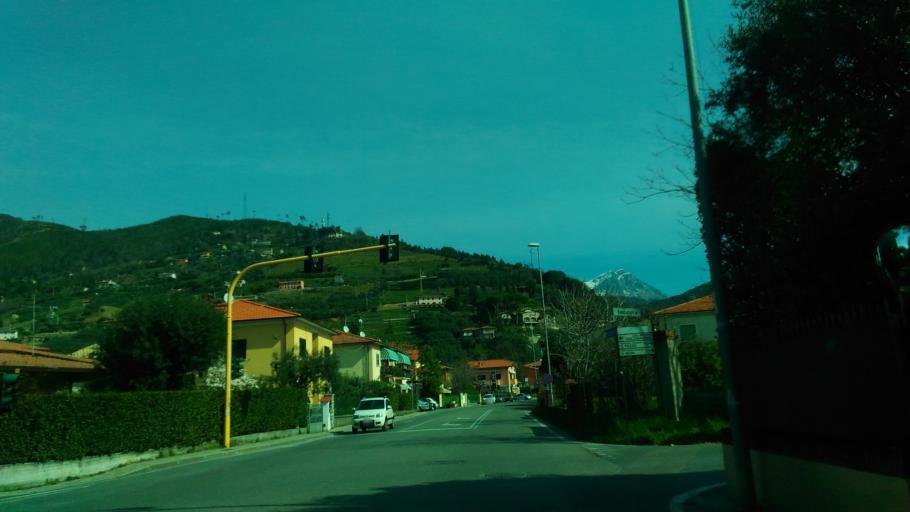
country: IT
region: Tuscany
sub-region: Provincia di Lucca
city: Ripa-Pozzi-Querceta-Ponterosso
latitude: 43.9836
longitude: 10.2102
